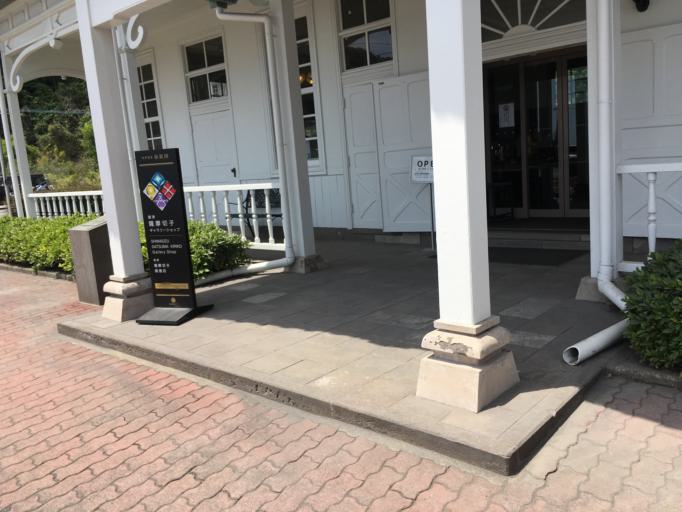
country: JP
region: Kagoshima
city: Kagoshima-shi
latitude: 31.6166
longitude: 130.5758
